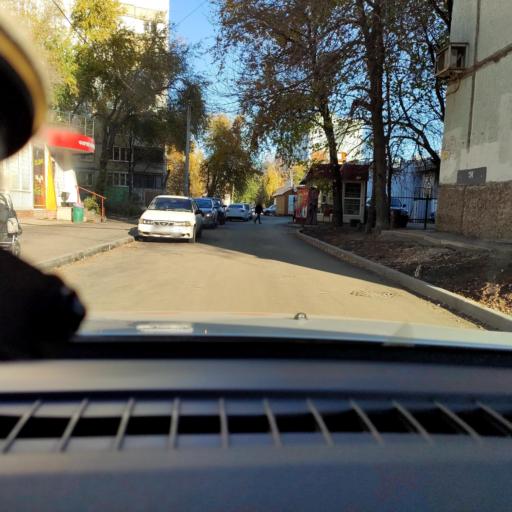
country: RU
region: Samara
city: Samara
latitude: 53.2392
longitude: 50.2070
